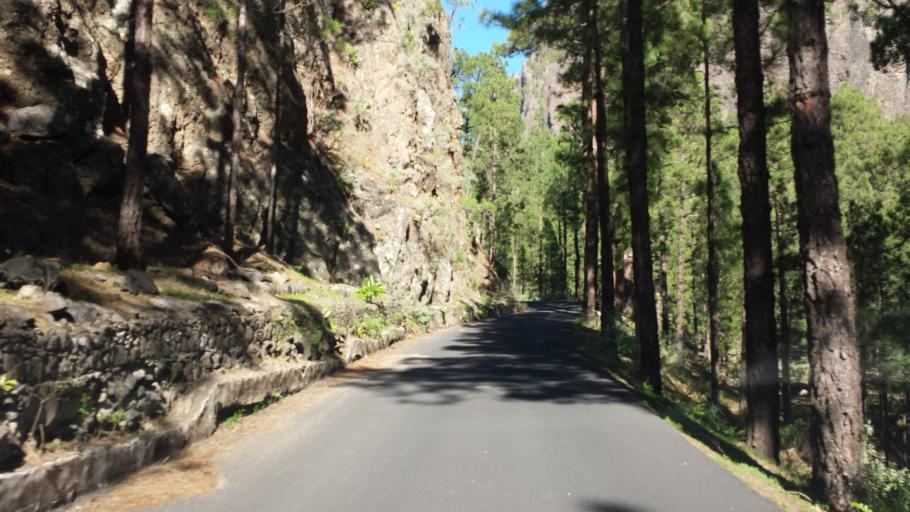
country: ES
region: Canary Islands
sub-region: Provincia de Santa Cruz de Tenerife
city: El Paso
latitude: 28.6857
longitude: -17.8485
